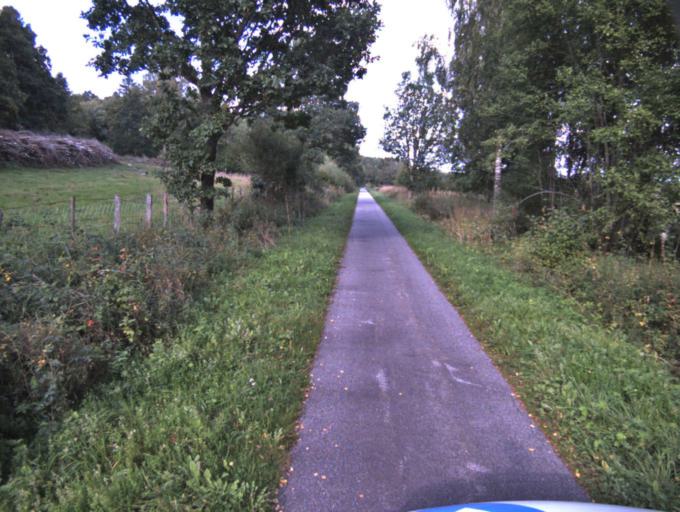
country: SE
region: Vaestra Goetaland
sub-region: Ulricehamns Kommun
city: Ulricehamn
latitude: 57.8903
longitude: 13.4372
